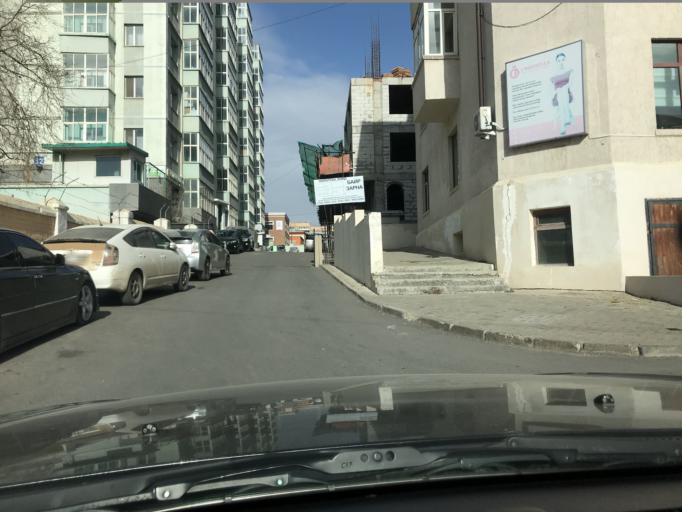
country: MN
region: Ulaanbaatar
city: Ulaanbaatar
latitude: 47.9190
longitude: 106.9393
